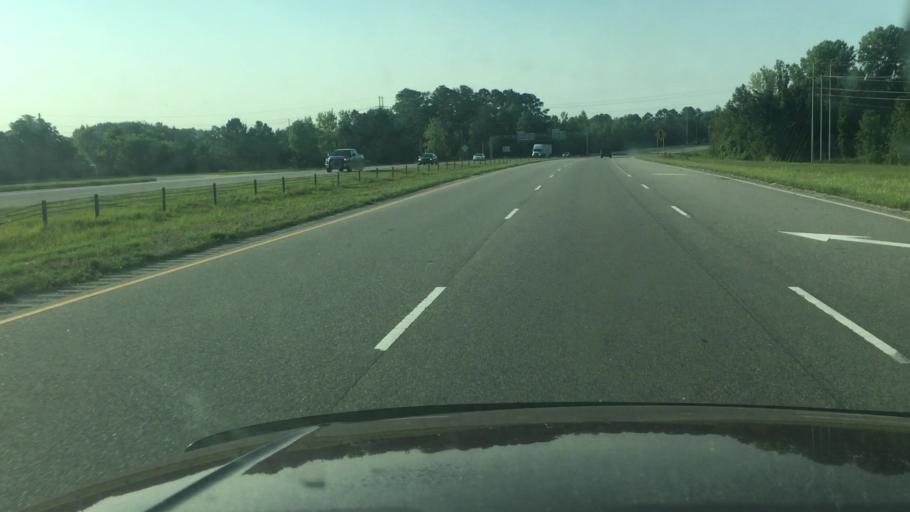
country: US
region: North Carolina
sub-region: Cumberland County
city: Fayetteville
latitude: 35.0323
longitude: -78.8767
